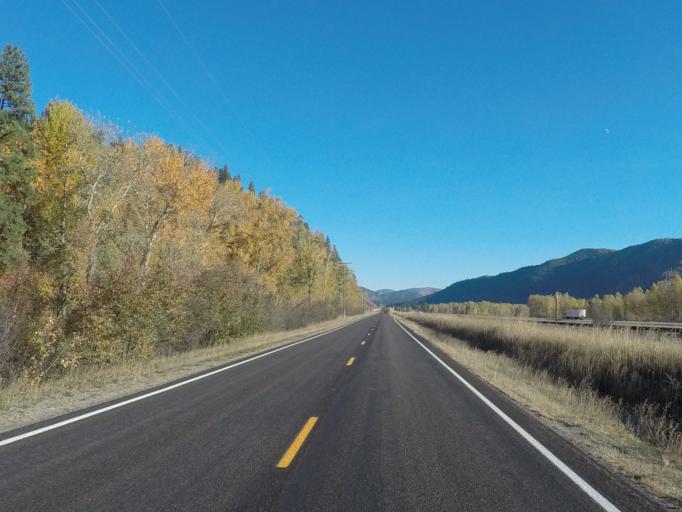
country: US
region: Montana
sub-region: Missoula County
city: Clinton
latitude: 46.8164
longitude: -113.7941
